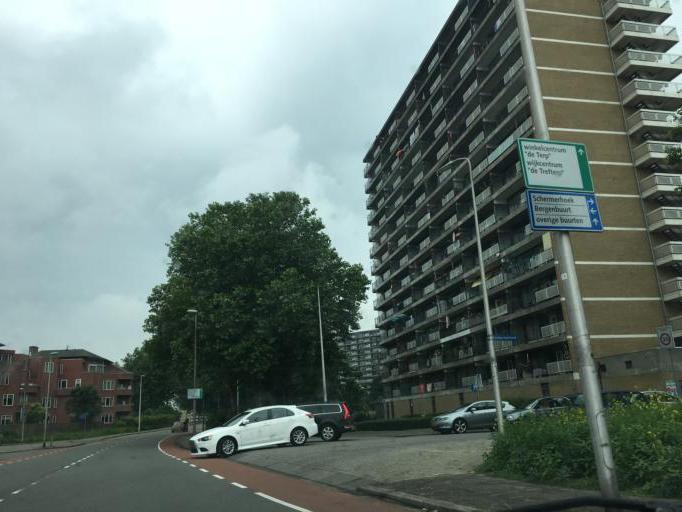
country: NL
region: South Holland
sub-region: Gemeente Krimpen aan den IJssel
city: Krimpen aan den IJssel
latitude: 51.9414
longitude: 4.6023
